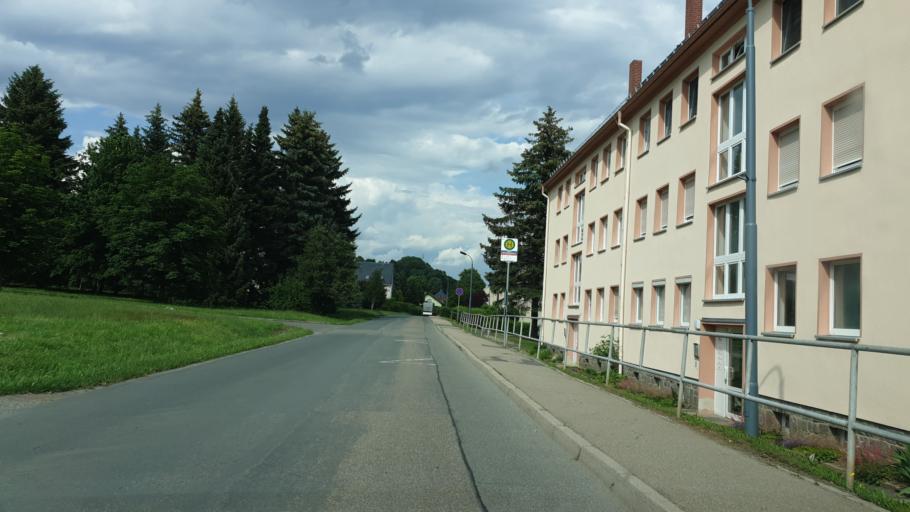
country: DE
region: Saxony
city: Lossnitz
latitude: 50.6181
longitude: 12.7223
